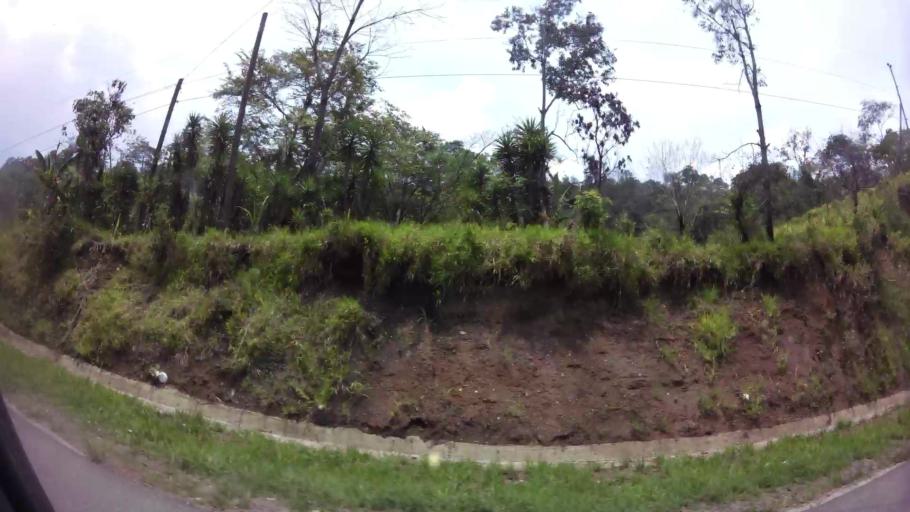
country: HN
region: Comayagua
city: Taulabe
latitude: 14.6795
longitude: -87.9568
